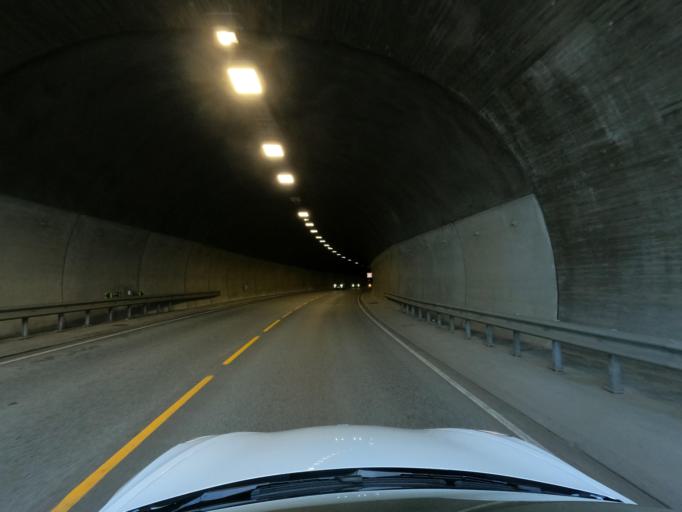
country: NO
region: Troms
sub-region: Harstad
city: Harstad
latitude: 68.8051
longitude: 16.5317
